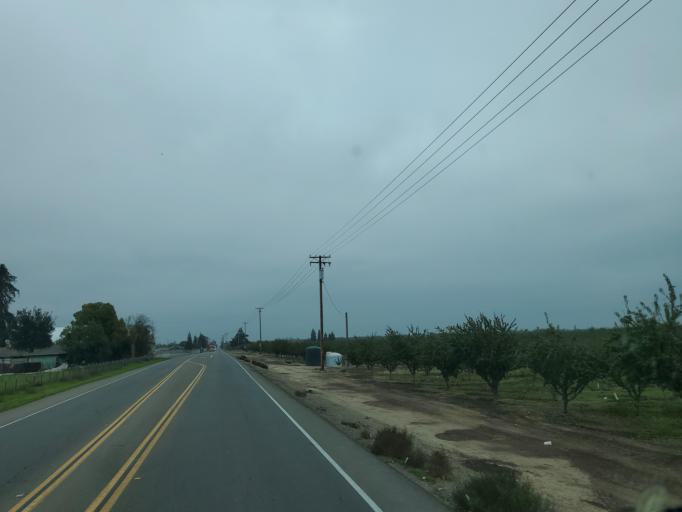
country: US
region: California
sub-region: Stanislaus County
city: Keyes
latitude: 37.5513
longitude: -120.8945
